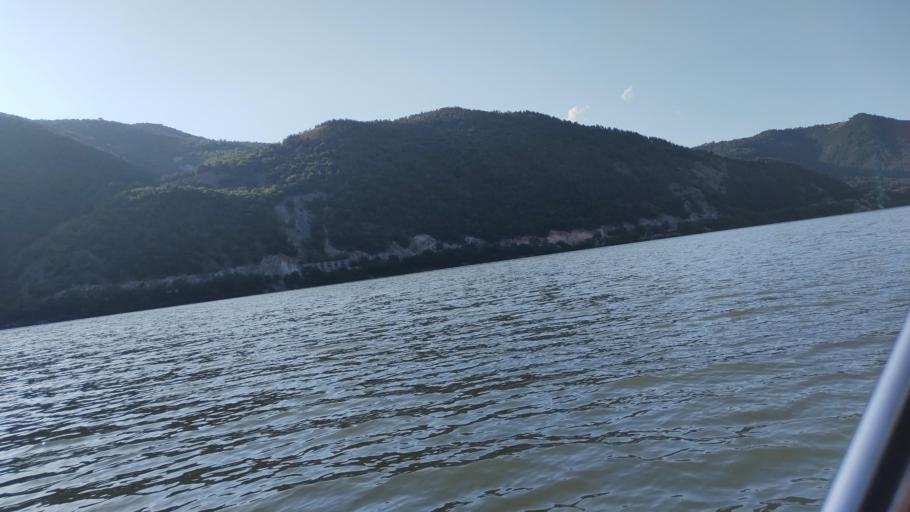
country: RO
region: Mehedinti
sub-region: Comuna Svinita
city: Svinita
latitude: 44.5046
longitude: 22.1945
